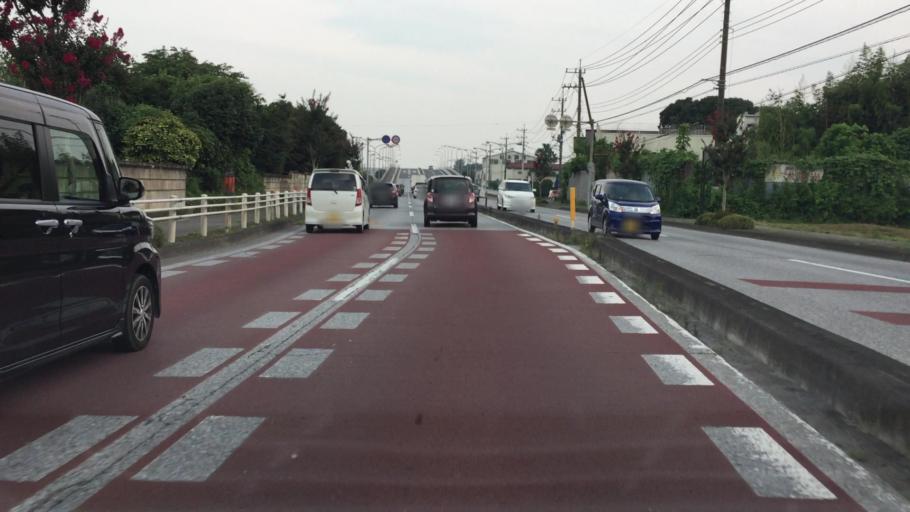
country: JP
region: Tochigi
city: Tochigi
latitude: 36.3675
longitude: 139.7160
